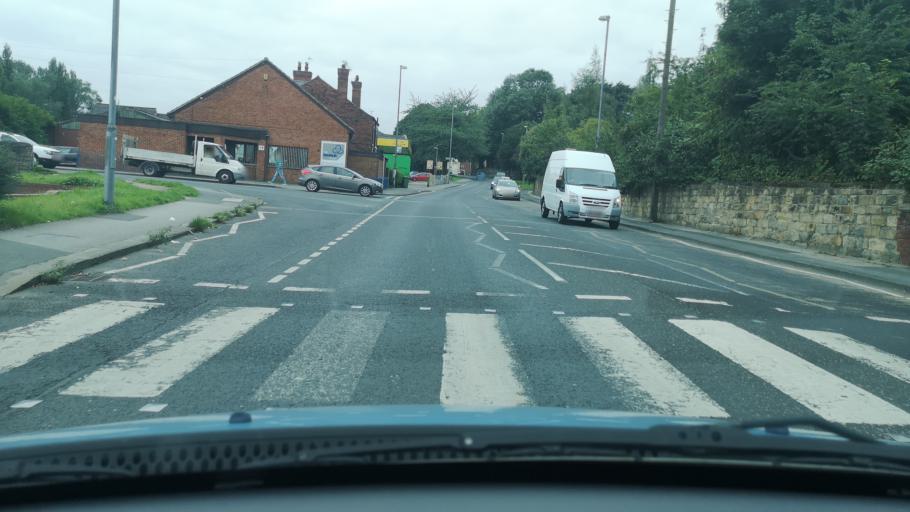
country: GB
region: England
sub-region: City and Borough of Wakefield
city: Pontefract
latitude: 53.6950
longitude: -1.3019
